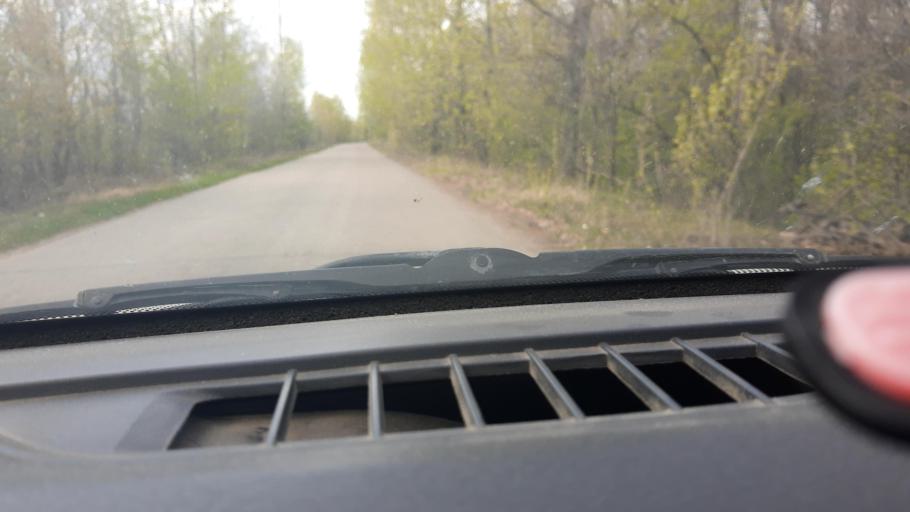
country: RU
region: Bashkortostan
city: Avdon
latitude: 54.6574
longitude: 55.8228
